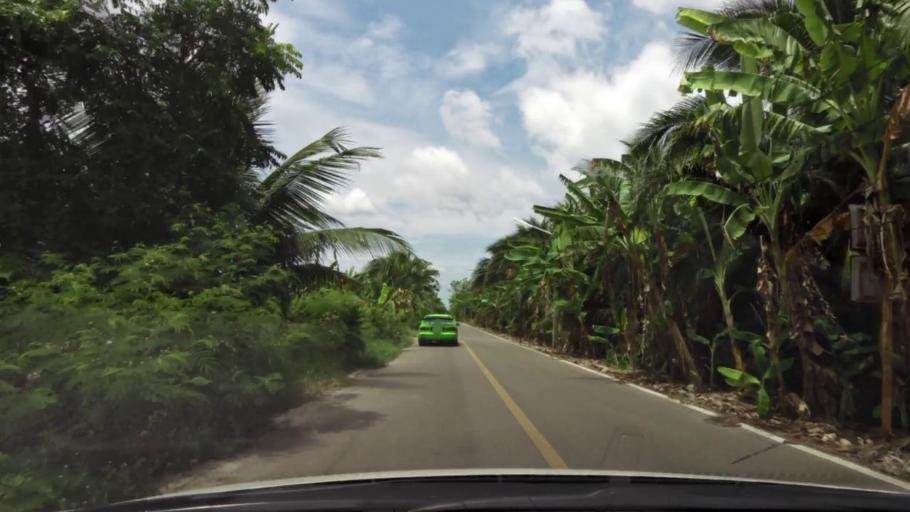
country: TH
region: Ratchaburi
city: Damnoen Saduak
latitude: 13.5275
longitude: 100.0134
